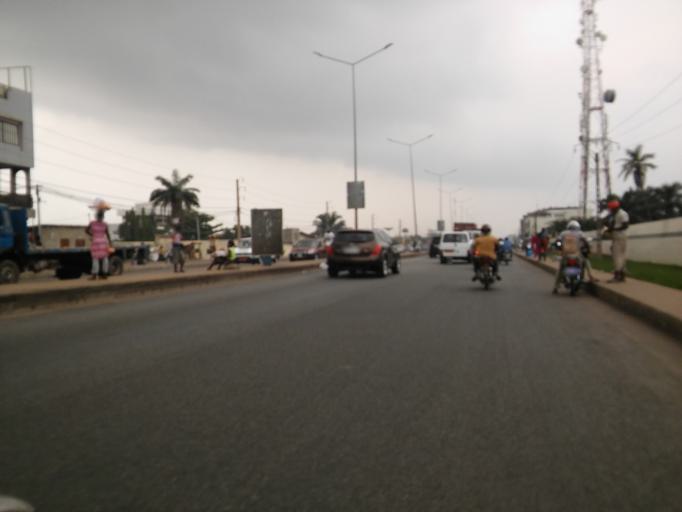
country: BJ
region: Littoral
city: Cotonou
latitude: 6.3774
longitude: 2.3859
